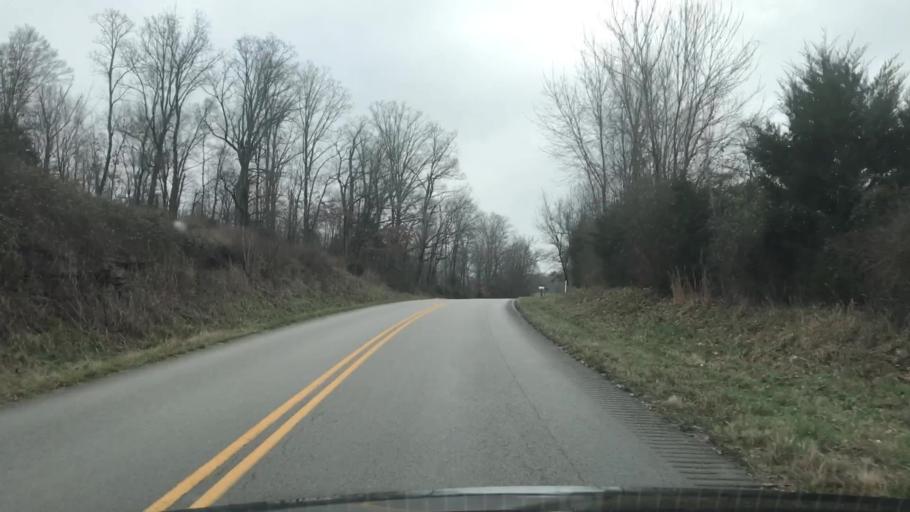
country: US
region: Kentucky
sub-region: Monroe County
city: Tompkinsville
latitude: 36.8499
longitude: -85.7698
